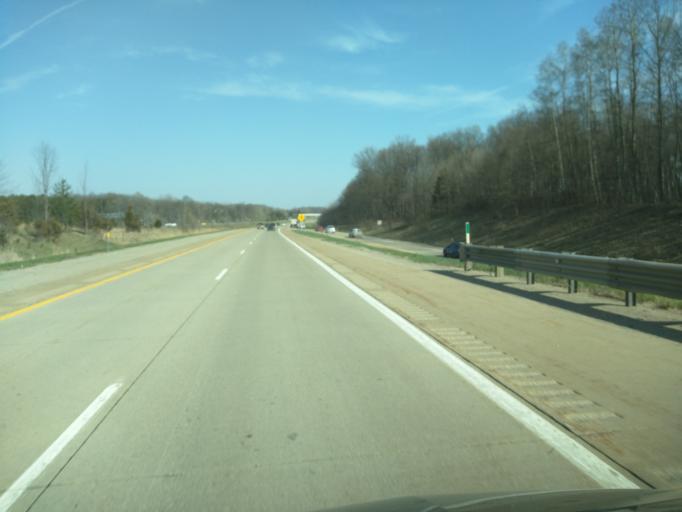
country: US
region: Michigan
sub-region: Kent County
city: Forest Hills
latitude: 42.8999
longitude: -85.5188
